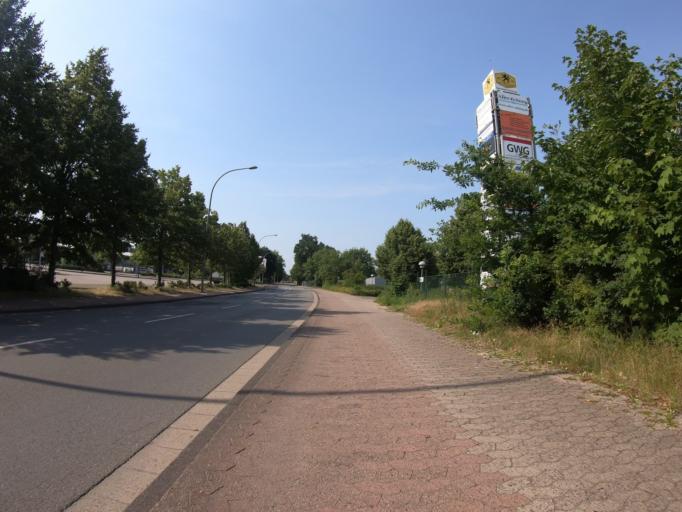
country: DE
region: Lower Saxony
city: Gifhorn
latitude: 52.4791
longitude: 10.5365
